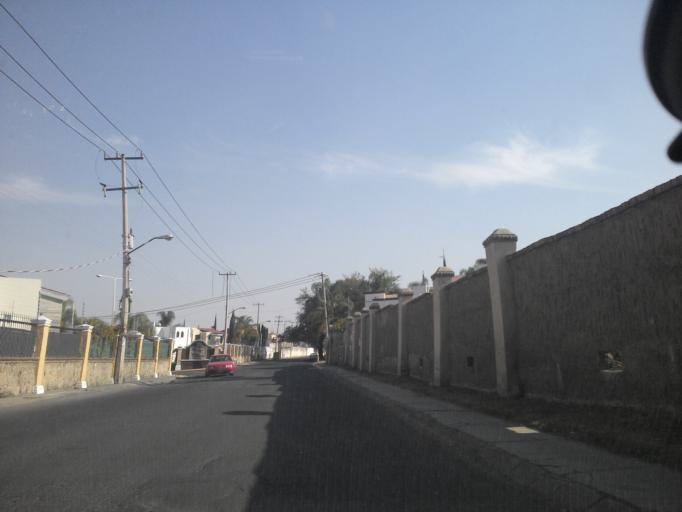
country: MX
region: Jalisco
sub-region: Tlajomulco de Zuniga
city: Palomar
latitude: 20.6091
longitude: -103.4526
